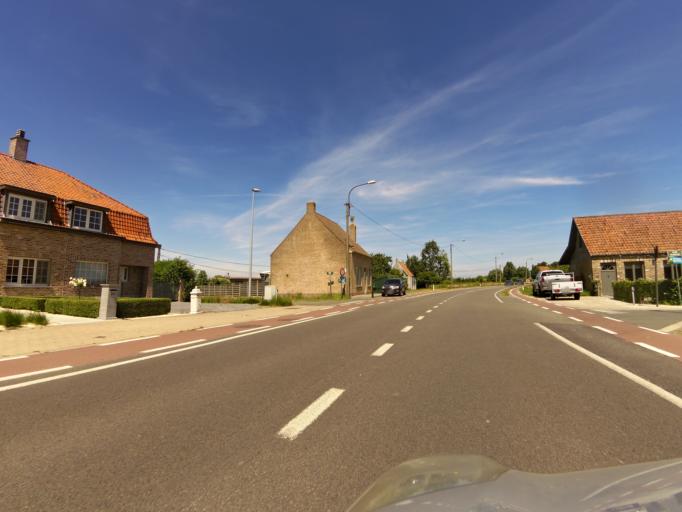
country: BE
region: Flanders
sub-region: Provincie West-Vlaanderen
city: Damme
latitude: 51.2819
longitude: 3.2344
